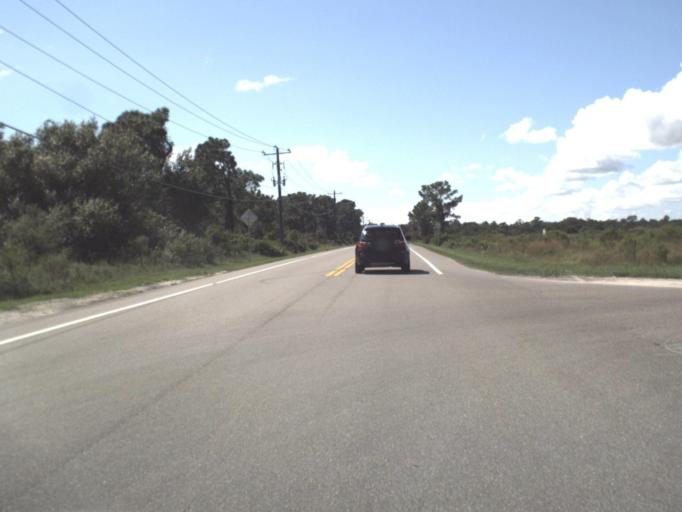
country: US
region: Florida
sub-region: Sarasota County
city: Lake Sarasota
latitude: 27.3872
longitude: -82.2711
